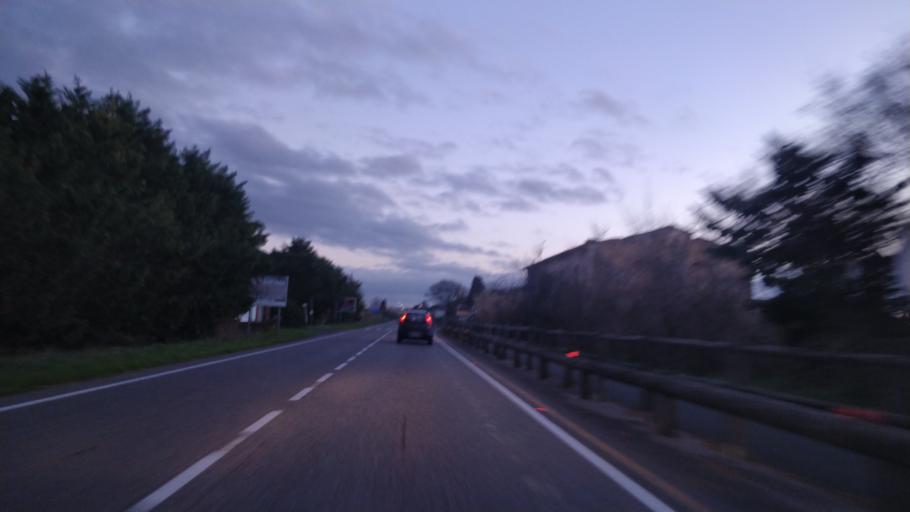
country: IT
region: Tuscany
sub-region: Provincia di Livorno
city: Vada
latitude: 43.3629
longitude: 10.4526
